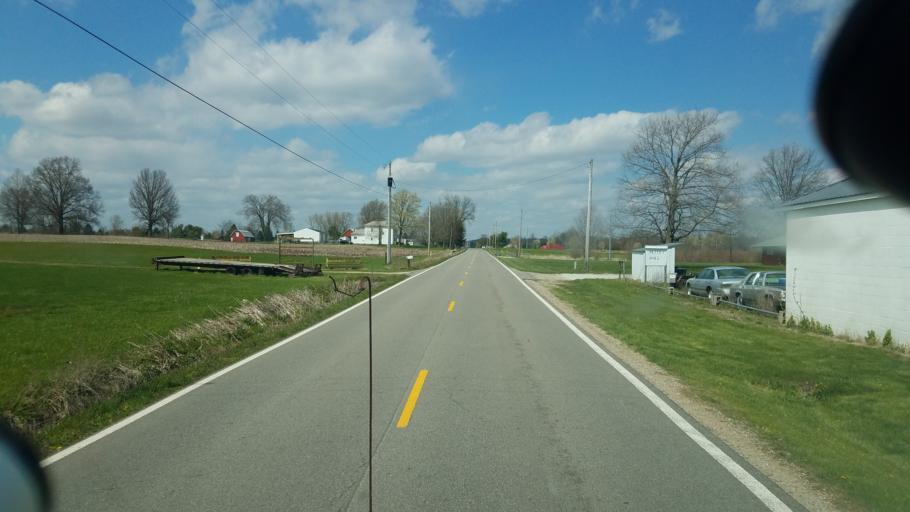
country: US
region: Ohio
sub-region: Licking County
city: Johnstown
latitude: 40.1069
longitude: -82.6165
